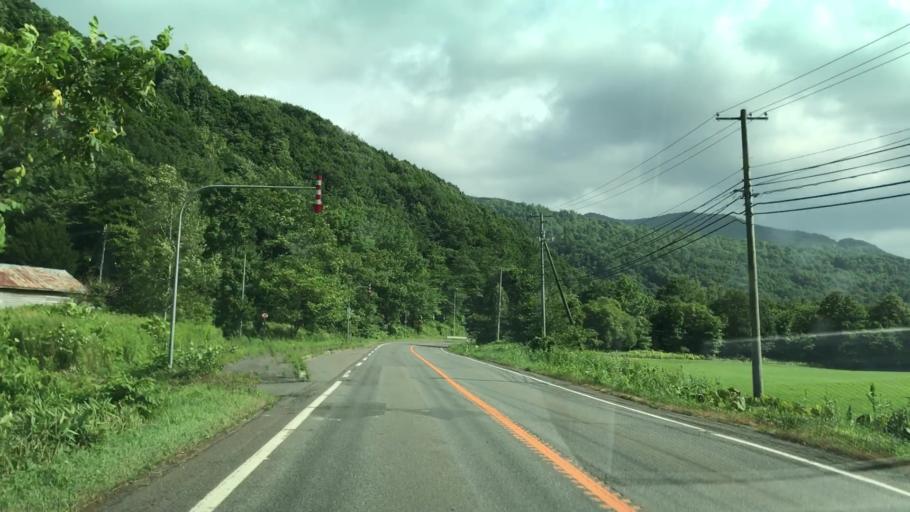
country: JP
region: Hokkaido
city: Shizunai-furukawacho
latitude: 42.8177
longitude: 142.4211
